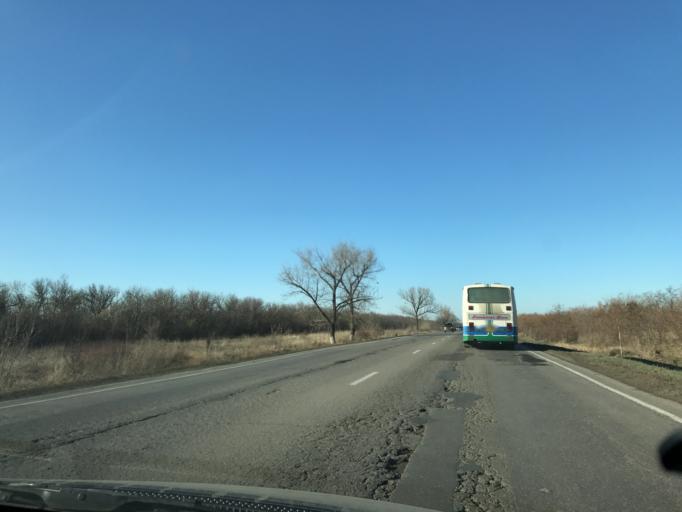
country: RU
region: Rostov
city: Kirovskaya
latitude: 47.0147
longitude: 39.9185
